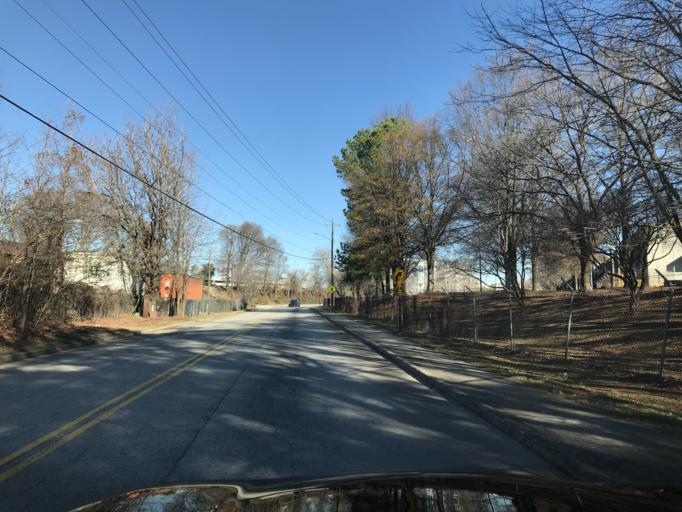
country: US
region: Georgia
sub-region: Fulton County
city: College Park
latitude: 33.6381
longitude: -84.4579
